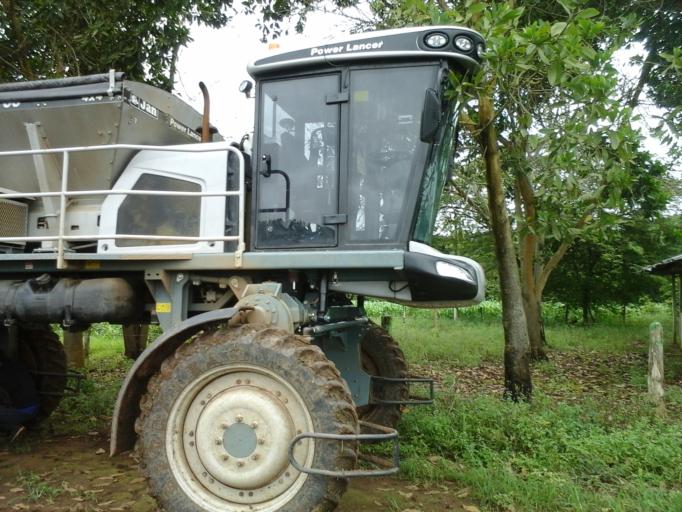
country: CO
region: Cundinamarca
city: Tibacuy
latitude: 4.2017
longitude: -72.4690
